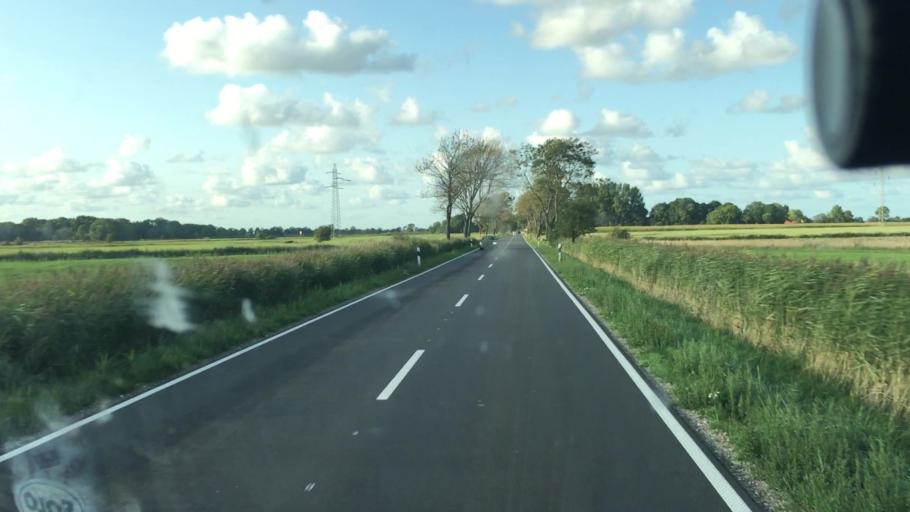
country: DE
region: Lower Saxony
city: Jever
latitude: 53.6337
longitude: 7.8614
